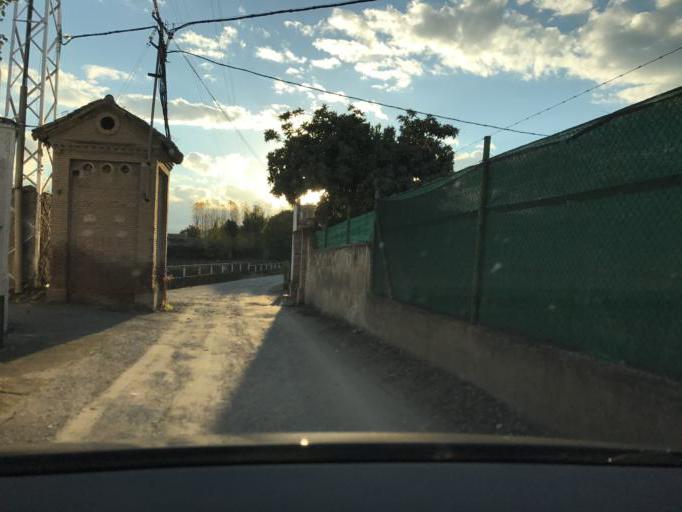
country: ES
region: Andalusia
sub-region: Provincia de Granada
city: Granada
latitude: 37.1685
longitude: -3.6132
